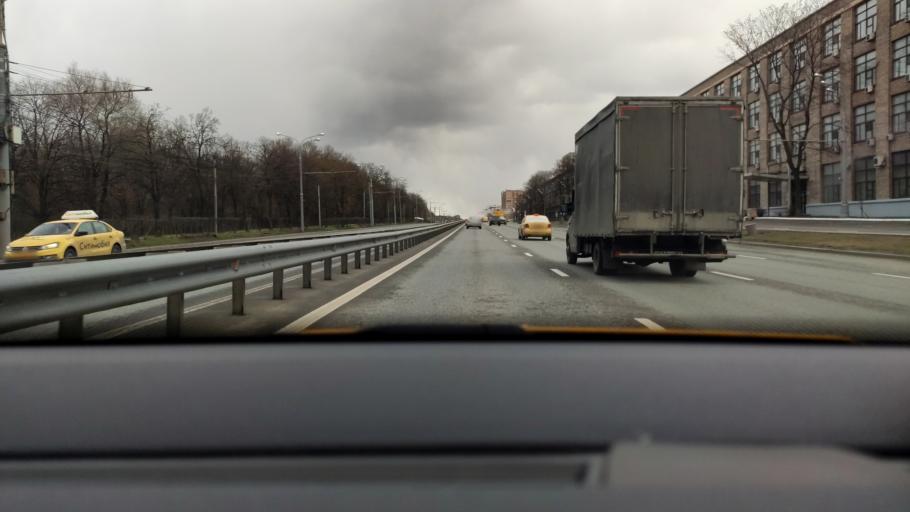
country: RU
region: Moscow
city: Ryazanskiy
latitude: 55.7598
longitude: 37.7627
